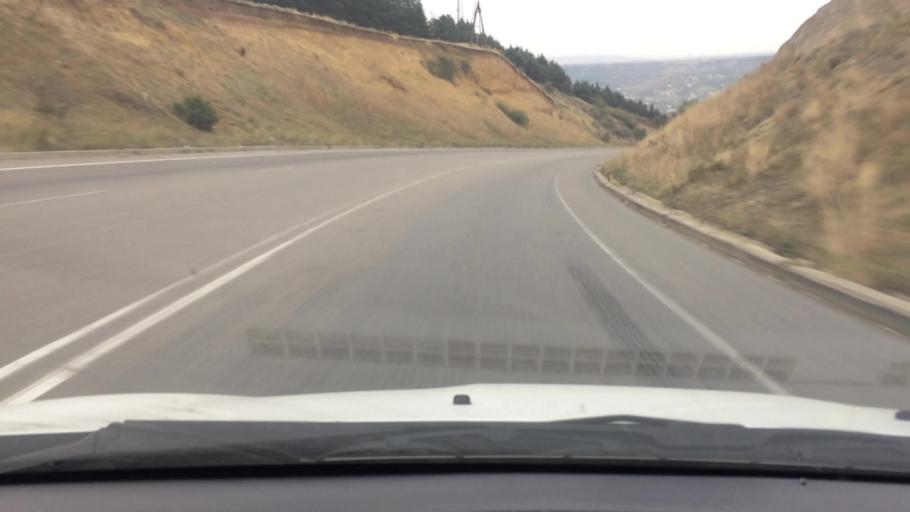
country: GE
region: T'bilisi
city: Tbilisi
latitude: 41.6259
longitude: 44.8057
